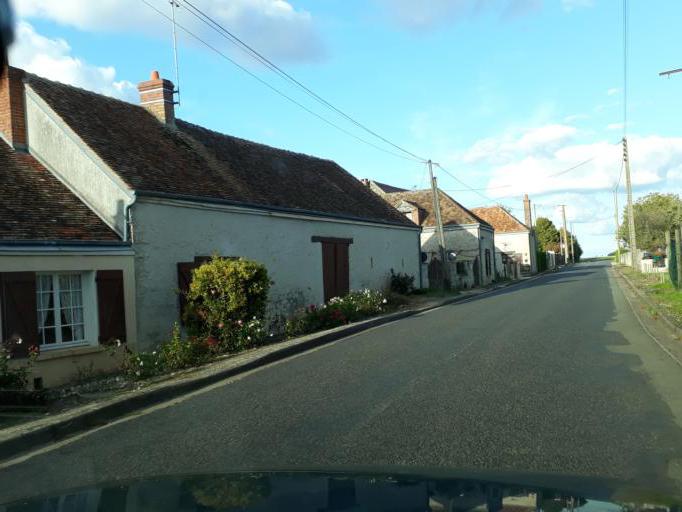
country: FR
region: Centre
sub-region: Departement du Loir-et-Cher
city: Ouzouer-le-Marche
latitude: 47.8252
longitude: 1.4994
